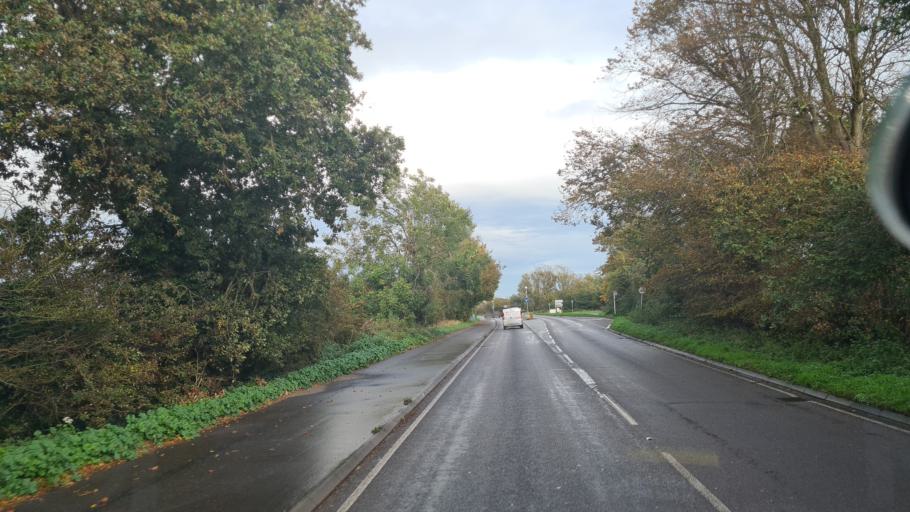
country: GB
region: England
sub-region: West Sussex
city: Littlehampton
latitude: 50.8087
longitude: -0.5710
